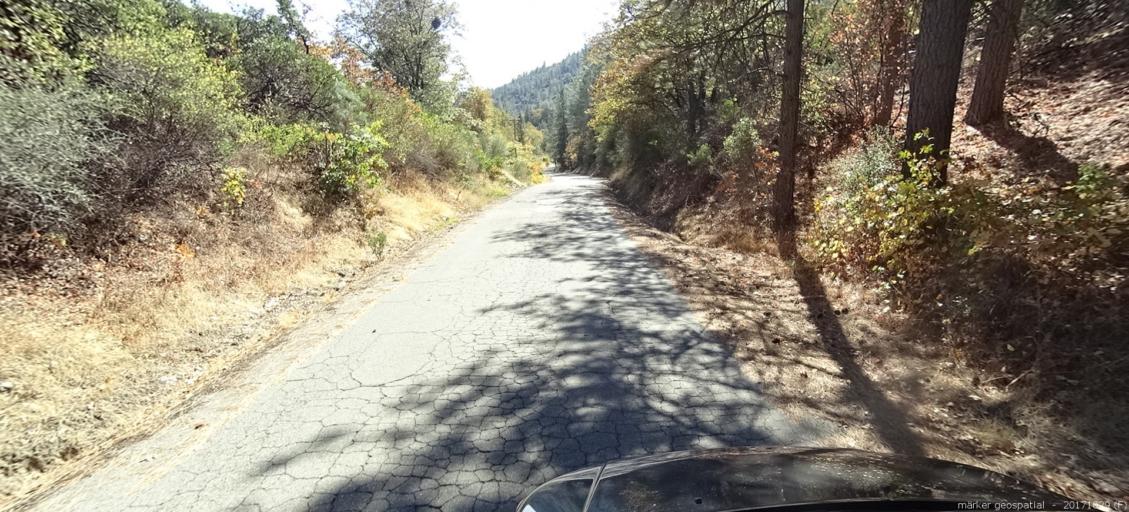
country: US
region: California
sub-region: Shasta County
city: Shasta
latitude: 40.4950
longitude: -122.6901
